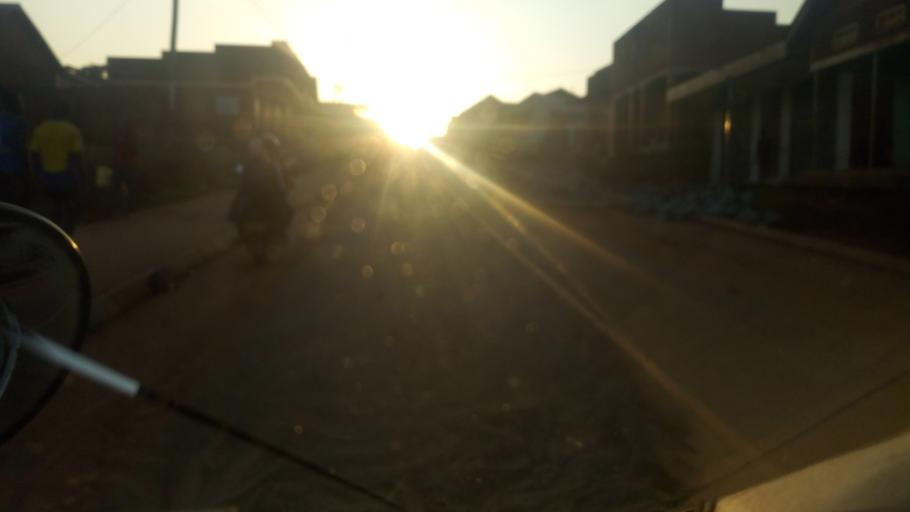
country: UG
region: Central Region
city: Kampala Central Division
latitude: 0.3610
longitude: 32.5573
